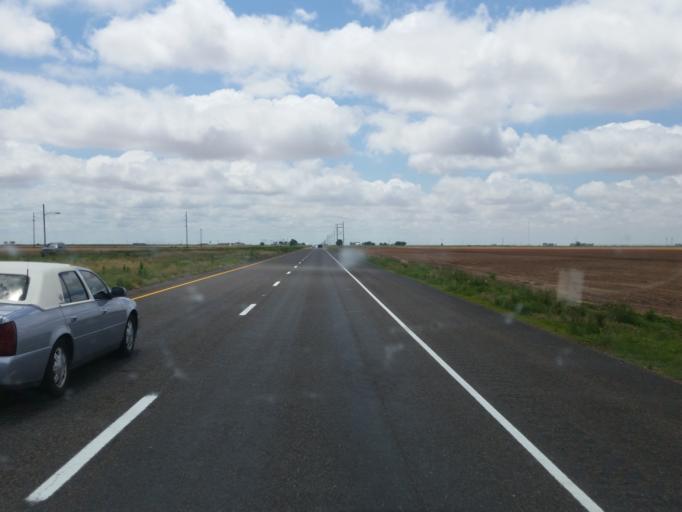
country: US
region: Texas
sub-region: Lubbock County
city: Slaton
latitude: 33.4113
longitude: -101.6286
